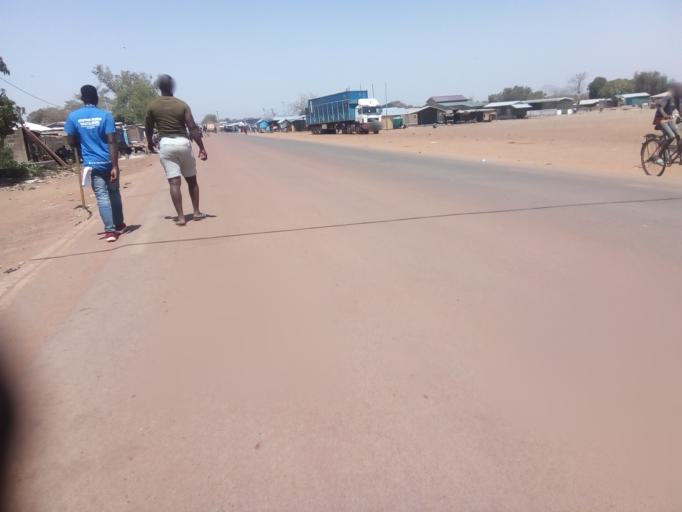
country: GH
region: Upper East
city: Navrongo
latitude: 11.0016
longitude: -1.1157
